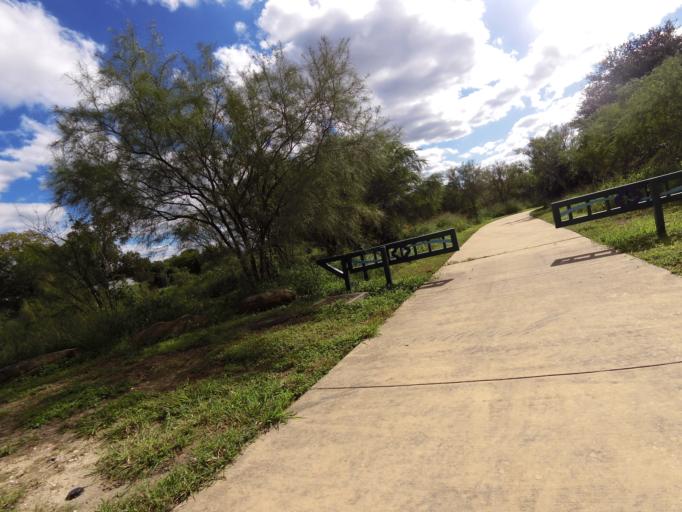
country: US
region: Texas
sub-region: Bexar County
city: San Antonio
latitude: 29.3932
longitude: -98.4952
